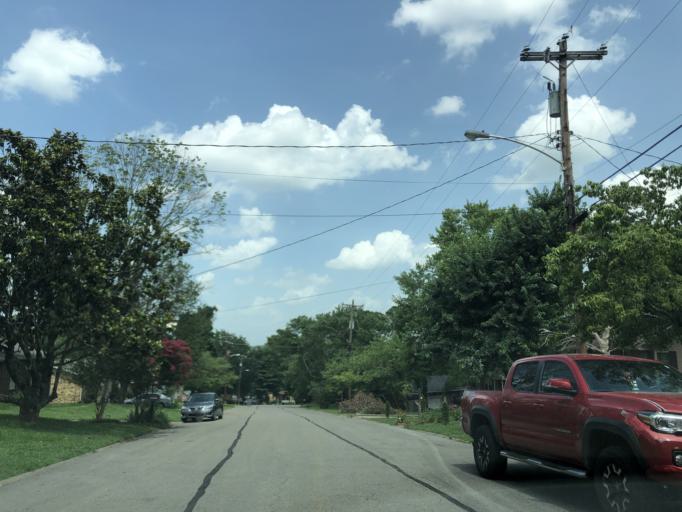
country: US
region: Tennessee
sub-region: Williamson County
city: Brentwood Estates
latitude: 36.0598
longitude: -86.6911
